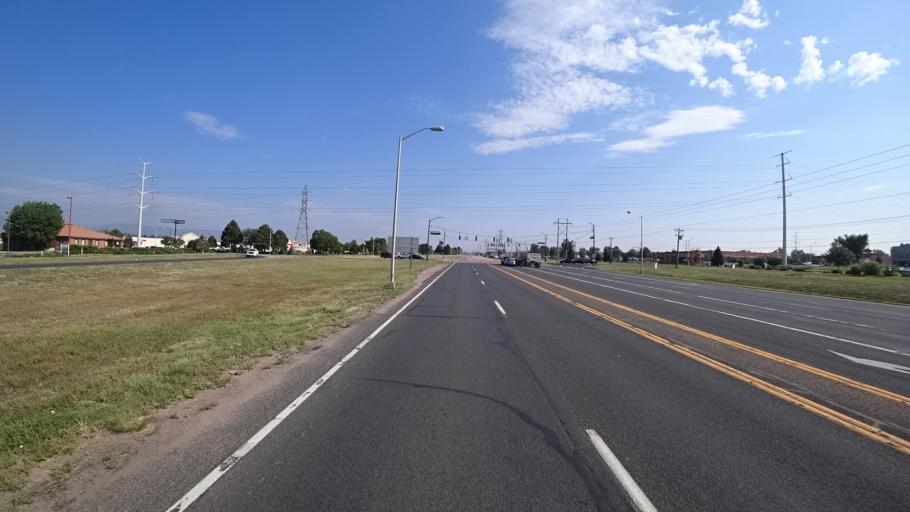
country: US
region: Colorado
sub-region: El Paso County
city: Stratmoor
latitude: 38.7881
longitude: -104.7577
